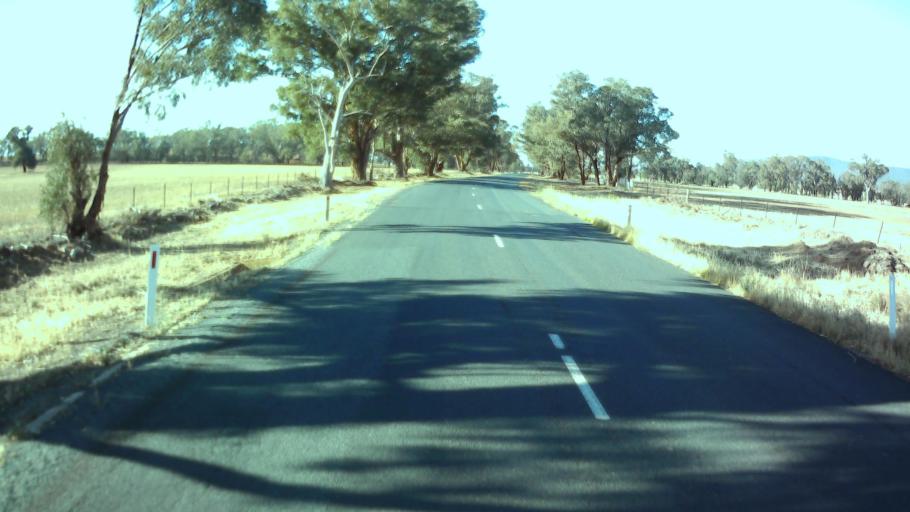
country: AU
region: New South Wales
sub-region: Weddin
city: Grenfell
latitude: -33.9381
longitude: 148.1373
